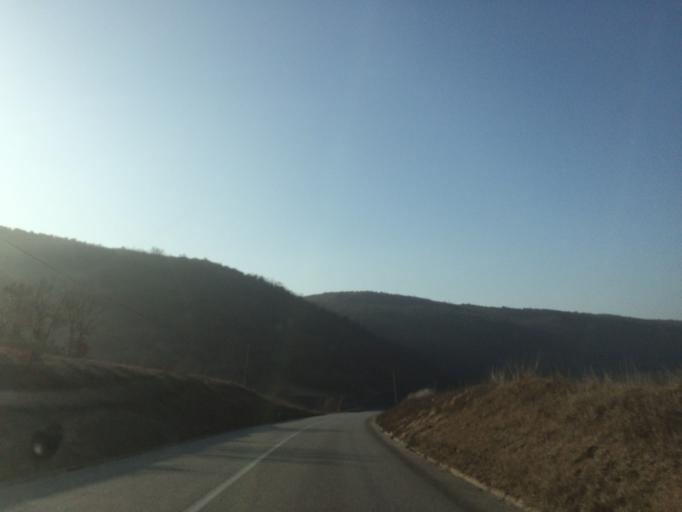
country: XK
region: Pec
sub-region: Komuna e Pejes
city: Kosuriq
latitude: 42.5094
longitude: 20.5460
